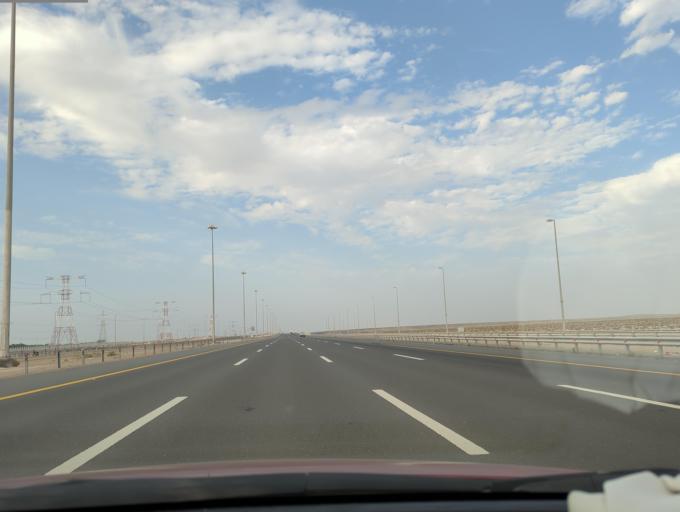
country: AE
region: Abu Dhabi
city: Abu Dhabi
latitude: 24.4614
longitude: 54.7496
